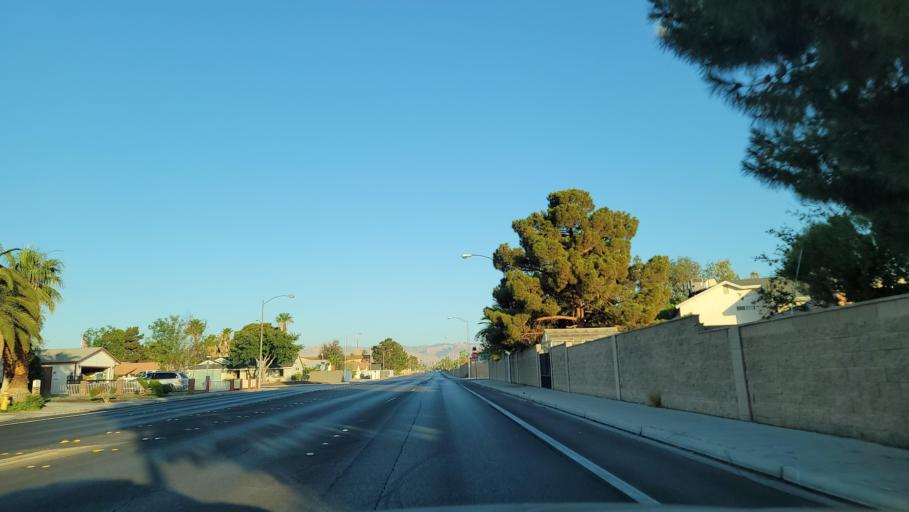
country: US
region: Nevada
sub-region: Clark County
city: Spring Valley
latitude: 36.1219
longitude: -115.2328
